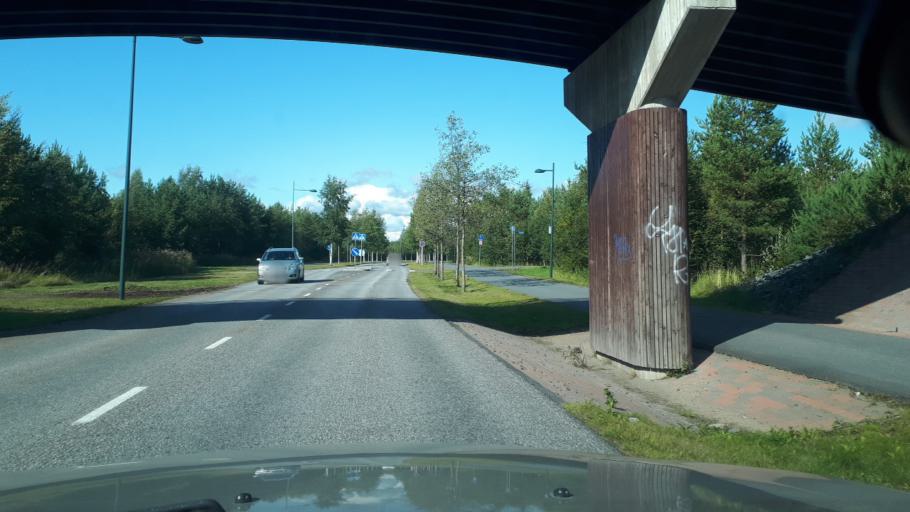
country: FI
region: Northern Ostrobothnia
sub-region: Oulu
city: Oulu
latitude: 65.0686
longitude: 25.4463
